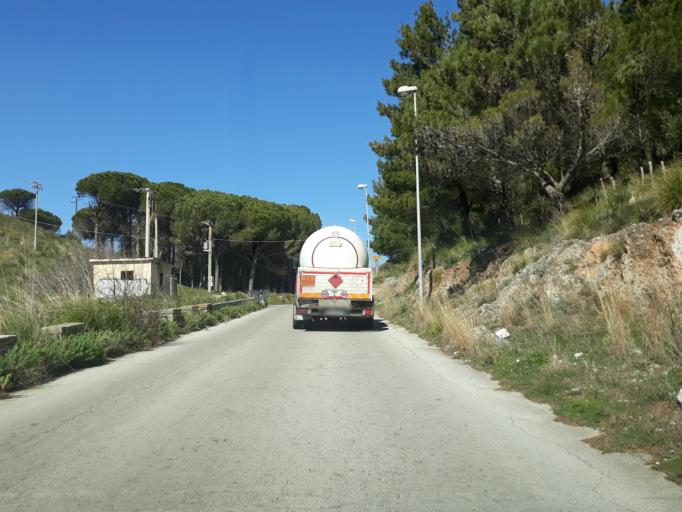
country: IT
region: Sicily
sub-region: Palermo
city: Piano dei Geli
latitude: 38.0817
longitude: 13.2718
